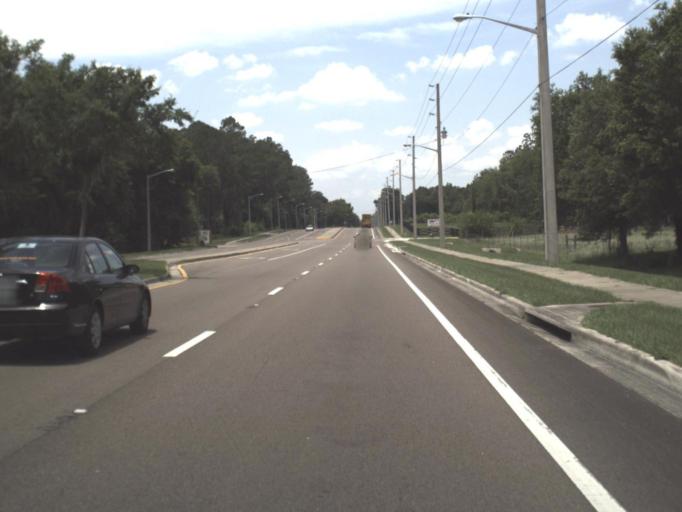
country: US
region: Florida
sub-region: Alachua County
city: Newberry
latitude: 29.6541
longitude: -82.5134
